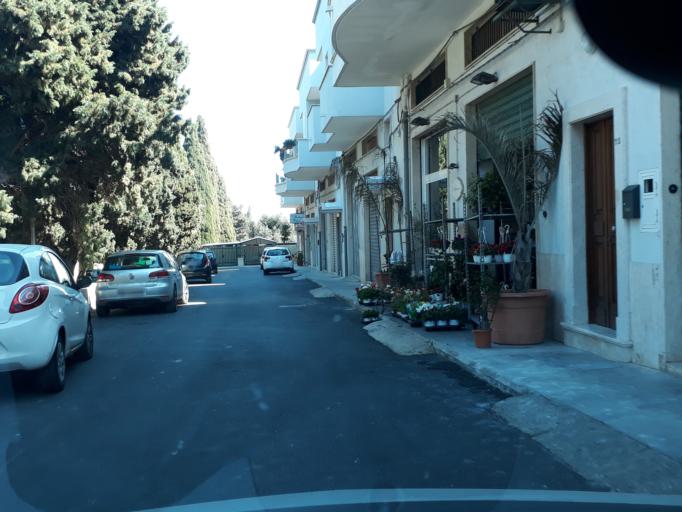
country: IT
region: Apulia
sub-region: Provincia di Brindisi
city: Fasano
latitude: 40.8382
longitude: 17.3638
